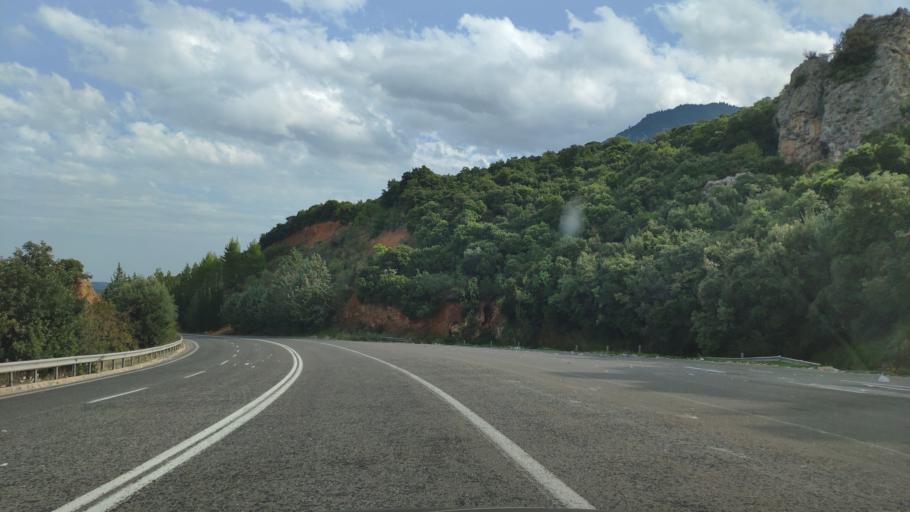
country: GR
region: Central Greece
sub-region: Nomos Fthiotidos
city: Anthili
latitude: 38.8011
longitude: 22.4977
